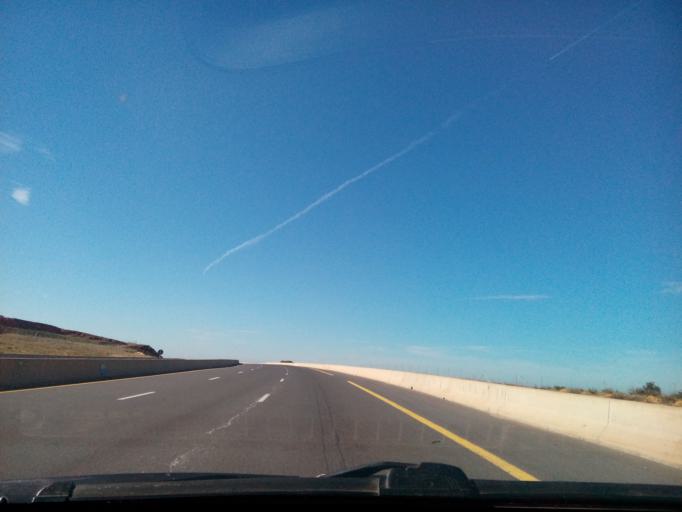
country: DZ
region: Tlemcen
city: Sidi Abdelli
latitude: 35.0200
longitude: -1.1422
